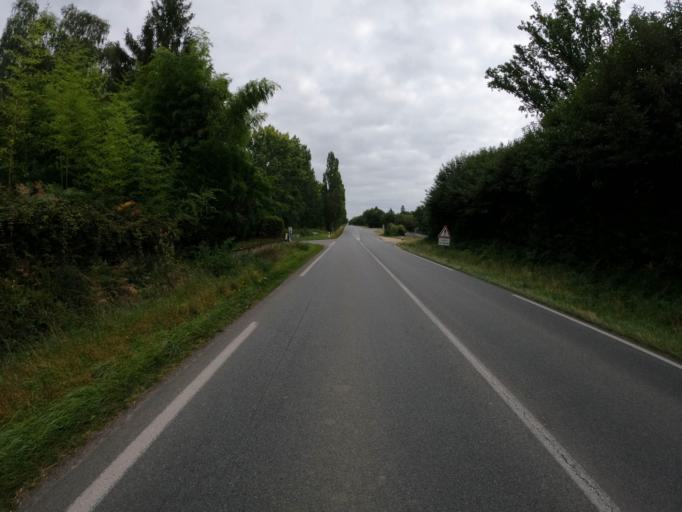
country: FR
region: Poitou-Charentes
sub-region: Departement des Deux-Sevres
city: Chef-Boutonne
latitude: 46.1826
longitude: -0.0307
